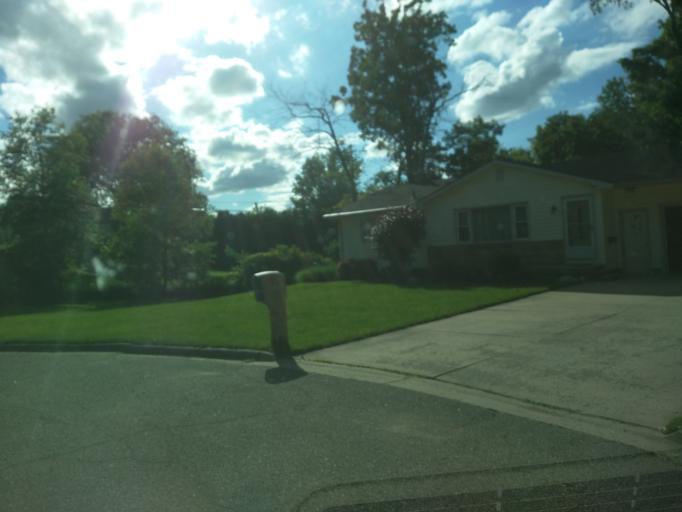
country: US
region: Michigan
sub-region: Eaton County
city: Waverly
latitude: 42.7516
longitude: -84.6171
